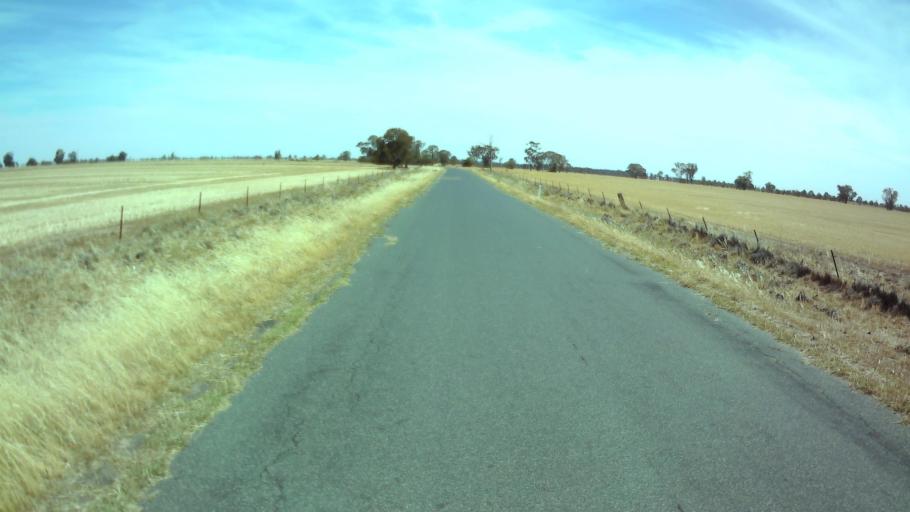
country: AU
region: New South Wales
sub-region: Weddin
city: Grenfell
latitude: -33.9338
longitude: 147.7618
